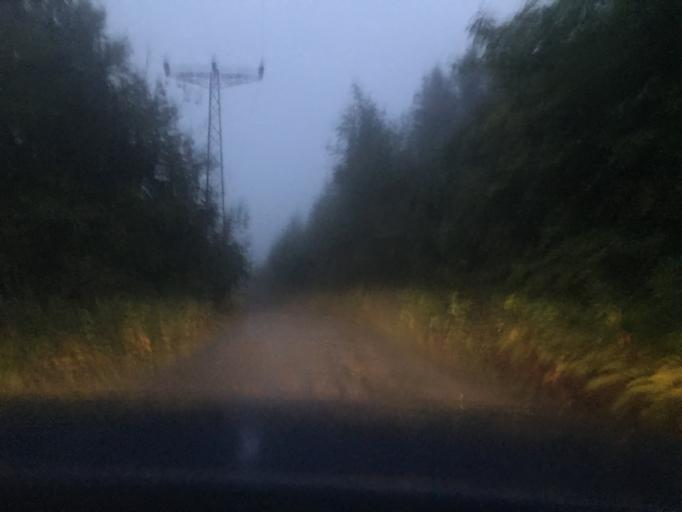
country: TR
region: Trabzon
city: Hayrat
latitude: 40.8291
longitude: 40.3881
